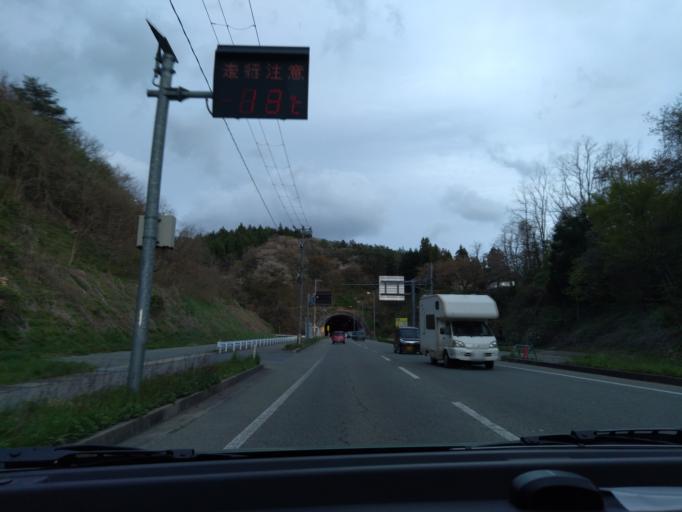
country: JP
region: Akita
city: Akita
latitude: 39.7450
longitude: 140.1334
